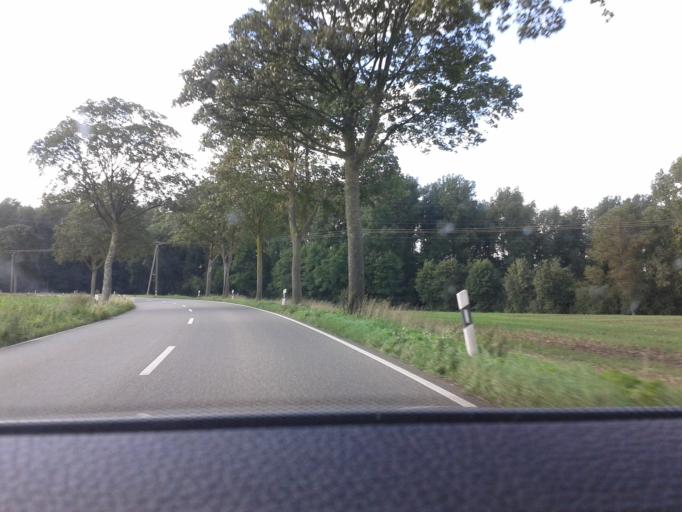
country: DE
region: North Rhine-Westphalia
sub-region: Regierungsbezirk Dusseldorf
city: Kevelaer
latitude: 51.6217
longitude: 6.2557
